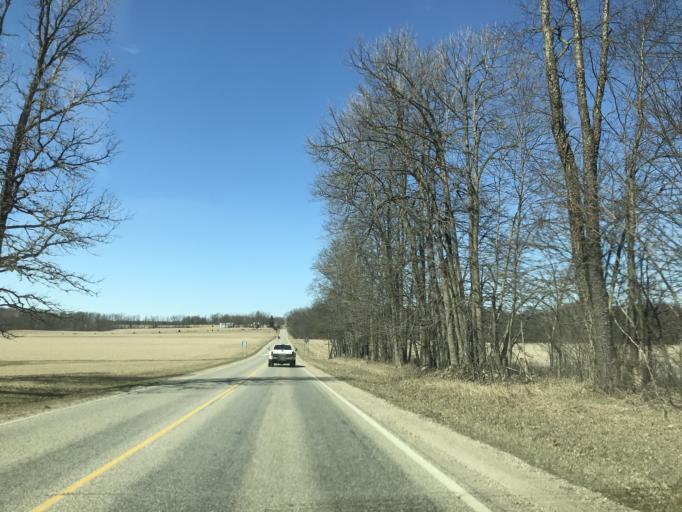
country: US
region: Michigan
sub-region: Hillsdale County
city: Litchfield
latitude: 41.9856
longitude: -84.7689
